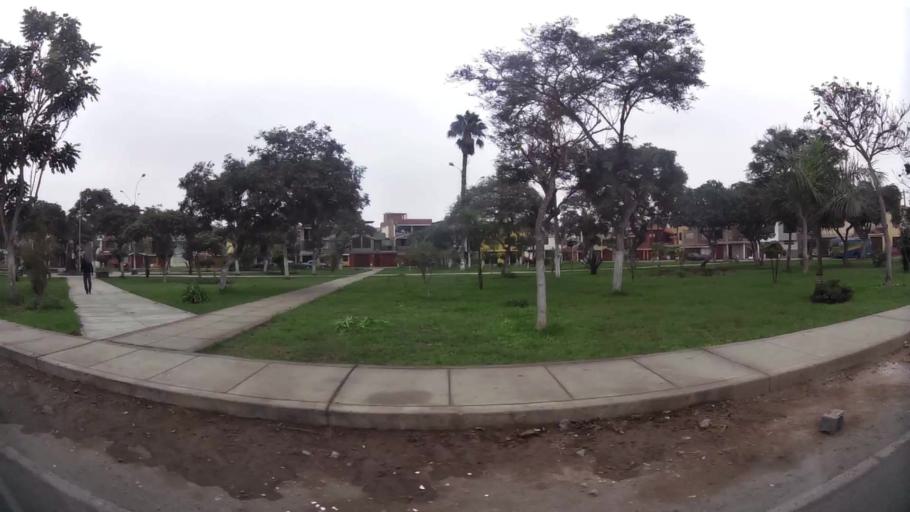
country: PE
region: Lima
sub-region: Lima
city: Surco
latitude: -12.1636
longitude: -76.9677
